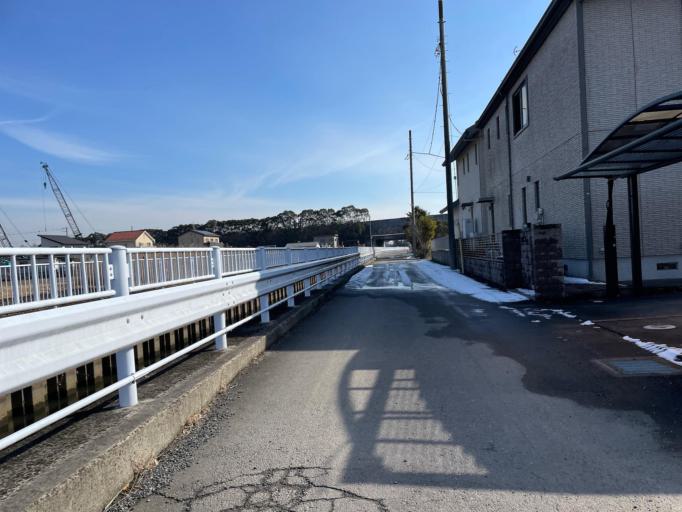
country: JP
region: Chiba
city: Nagareyama
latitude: 35.8584
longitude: 139.8773
